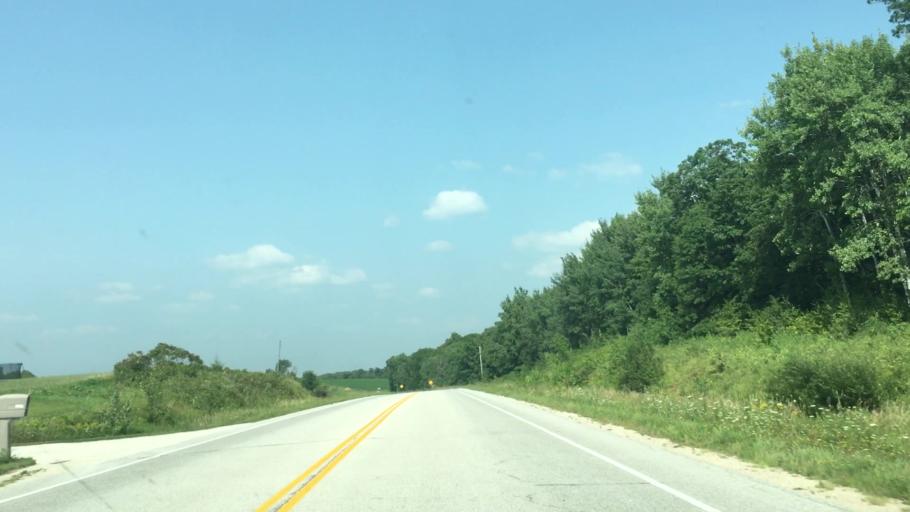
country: US
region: Minnesota
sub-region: Fillmore County
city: Harmony
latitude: 43.6435
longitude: -91.9279
